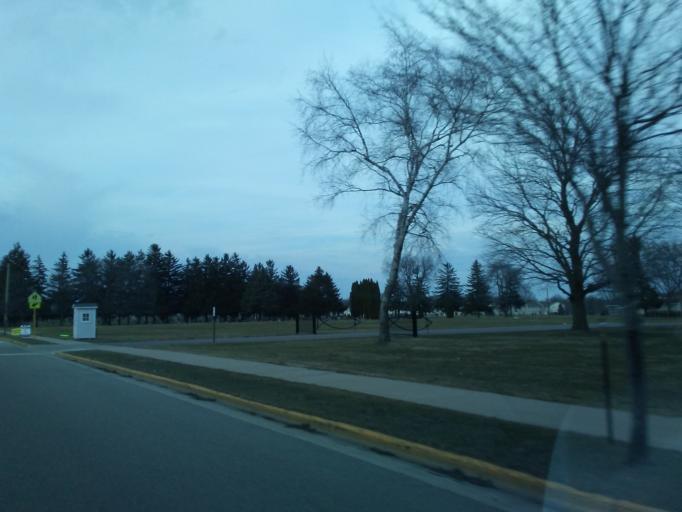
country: US
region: Wisconsin
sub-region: Dane County
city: Verona
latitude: 42.9949
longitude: -89.5336
